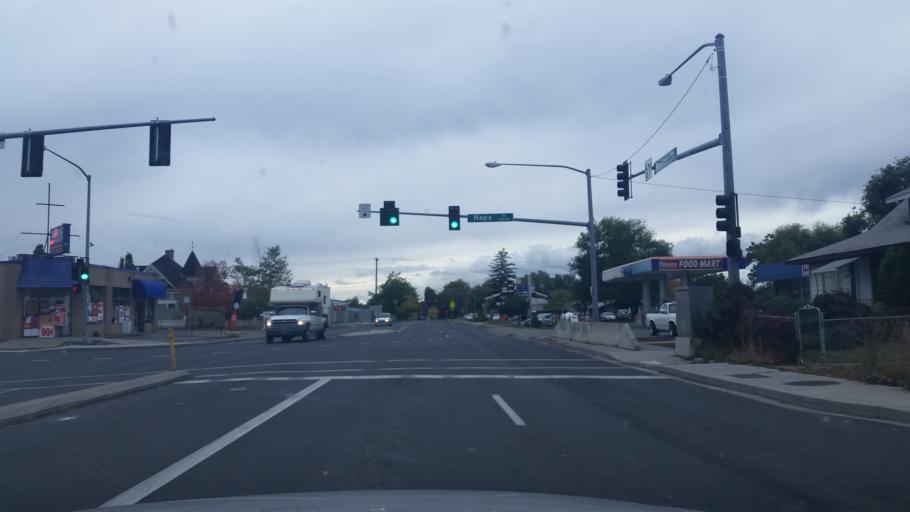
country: US
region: Washington
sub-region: Spokane County
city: Spokane
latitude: 47.6719
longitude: -117.3808
